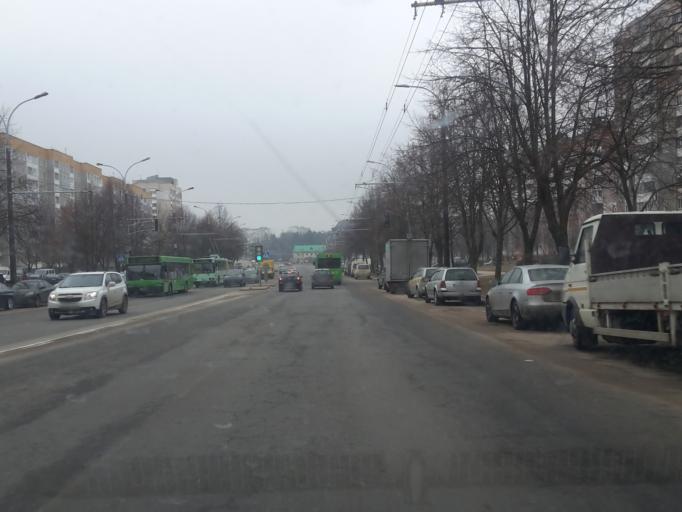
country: BY
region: Minsk
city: Novoye Medvezhino
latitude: 53.8992
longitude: 27.4349
